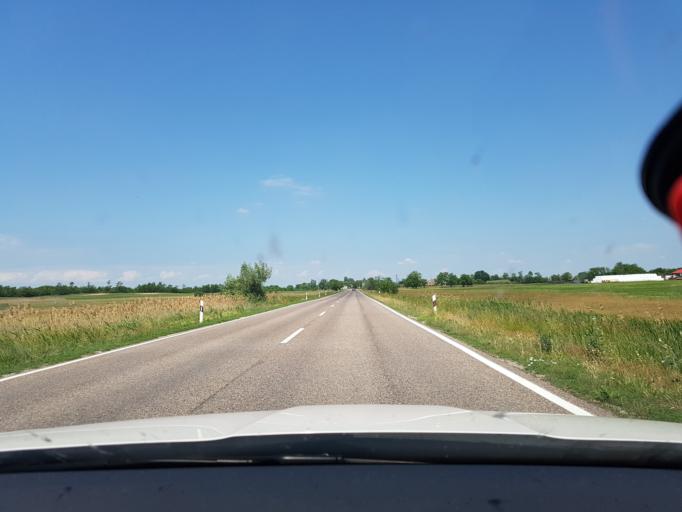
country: HU
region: Hajdu-Bihar
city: Egyek
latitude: 47.5844
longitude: 20.8536
